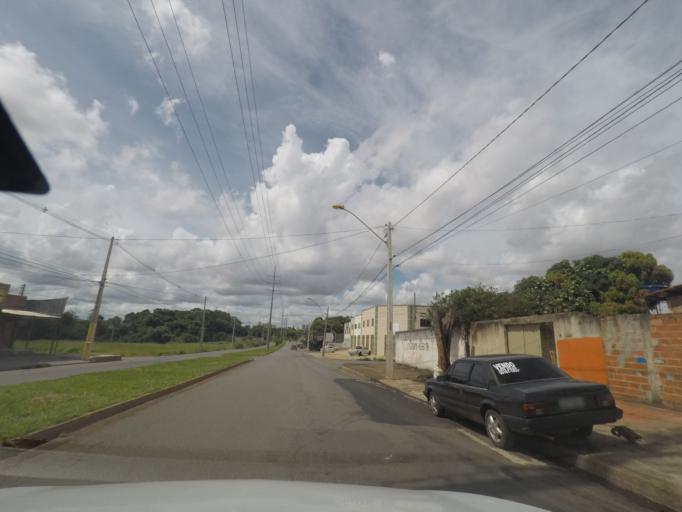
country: BR
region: Goias
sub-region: Goiania
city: Goiania
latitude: -16.7221
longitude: -49.3367
